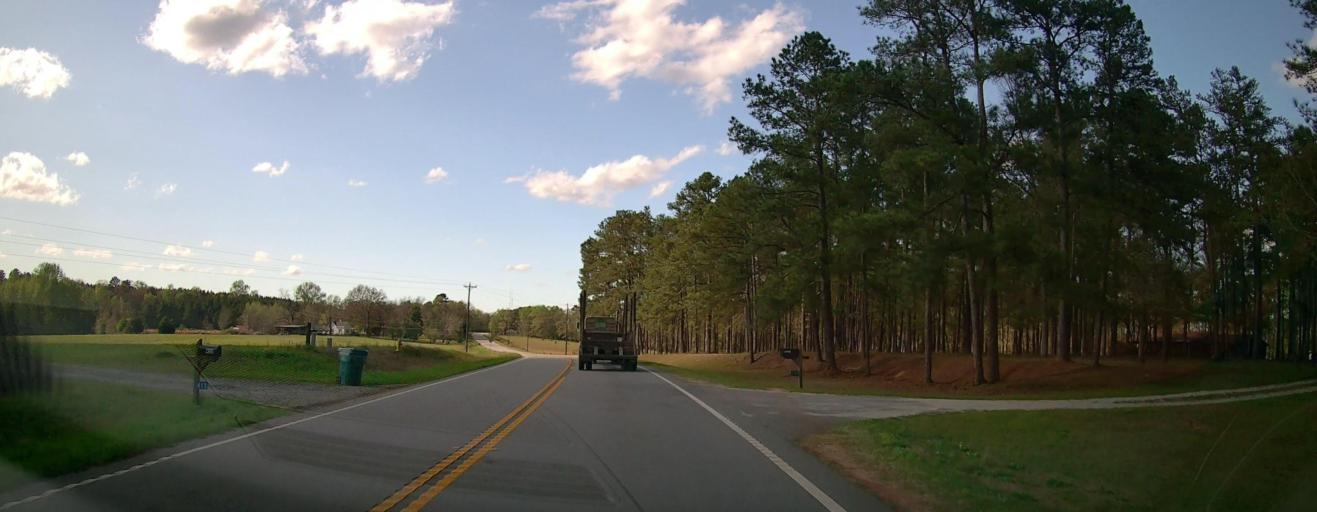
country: US
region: Georgia
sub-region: Baldwin County
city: Hardwick
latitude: 33.0553
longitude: -83.1248
